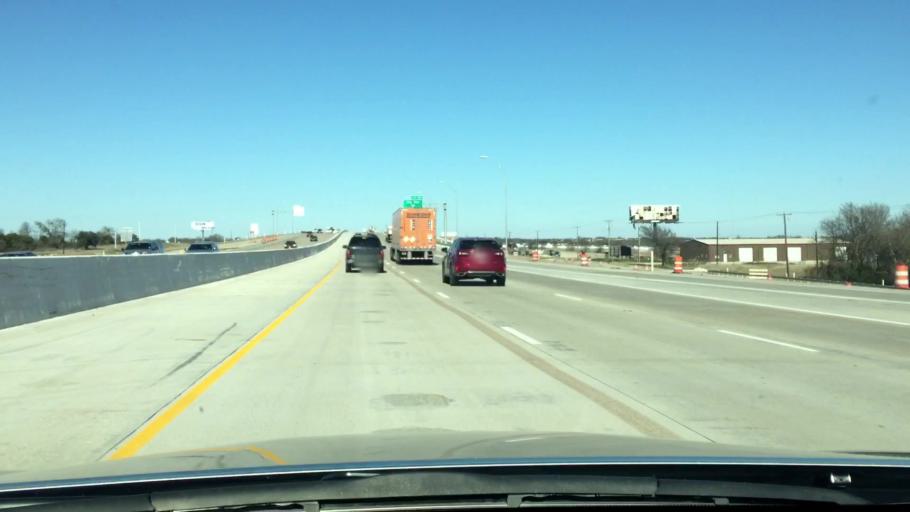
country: US
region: Texas
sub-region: Bell County
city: Troy
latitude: 31.2141
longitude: -97.2996
